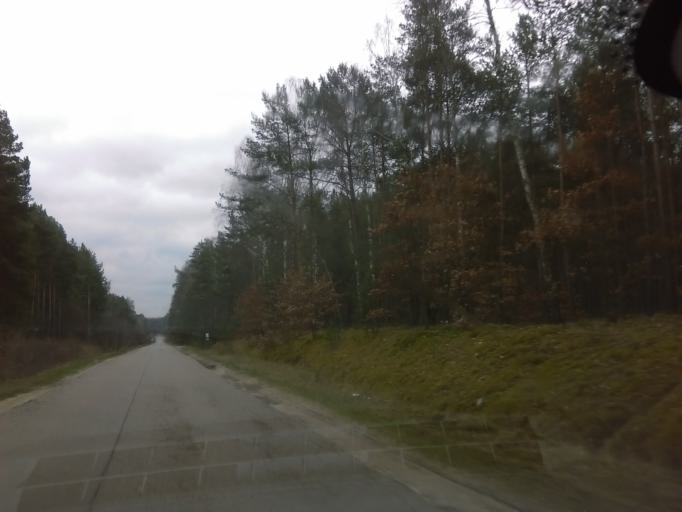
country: PL
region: Kujawsko-Pomorskie
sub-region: Powiat sepolenski
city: Sypniewo
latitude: 53.4562
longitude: 17.3418
